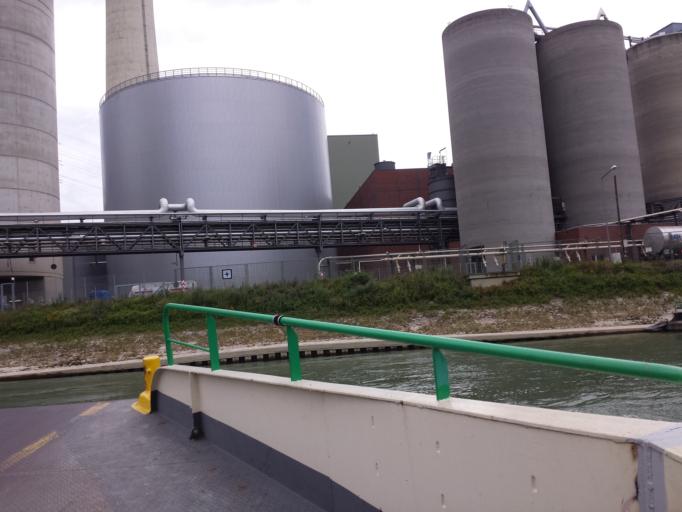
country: DE
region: Rheinland-Pfalz
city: Altrip
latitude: 49.4422
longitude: 8.5023
